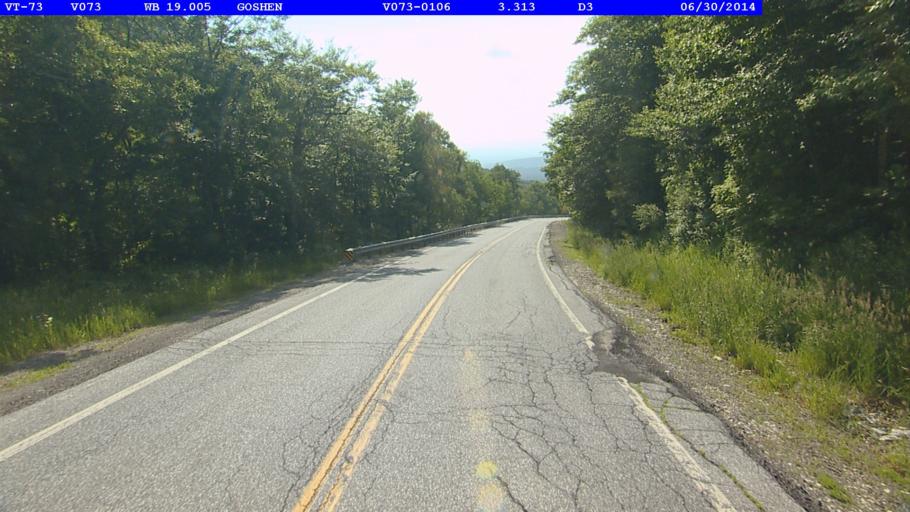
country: US
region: Vermont
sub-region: Rutland County
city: Brandon
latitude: 43.8400
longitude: -72.9698
